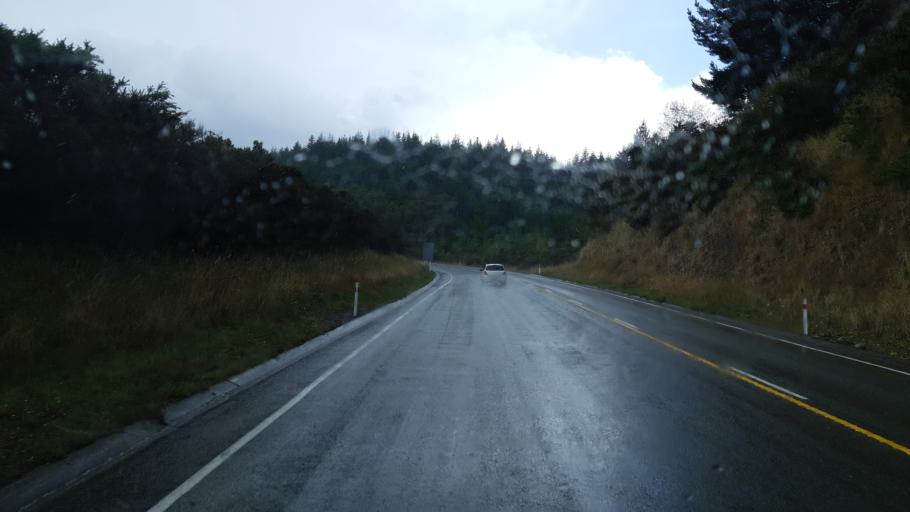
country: NZ
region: Tasman
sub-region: Tasman District
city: Wakefield
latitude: -41.4850
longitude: 172.9036
